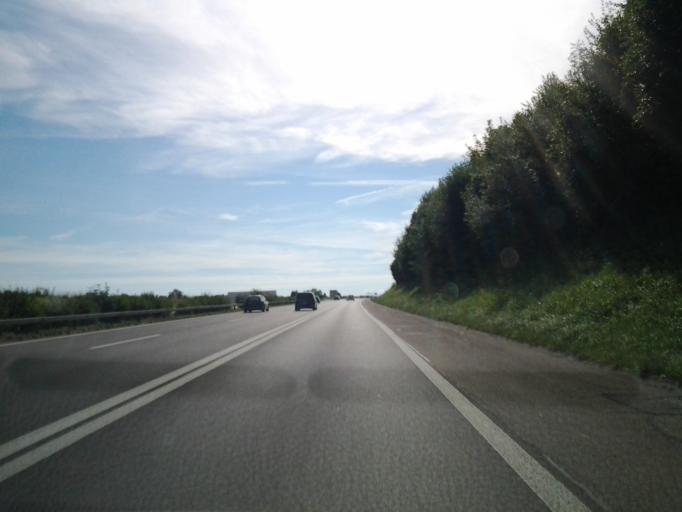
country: CH
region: Zurich
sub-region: Bezirk Horgen
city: Au
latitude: 47.2302
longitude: 8.6360
